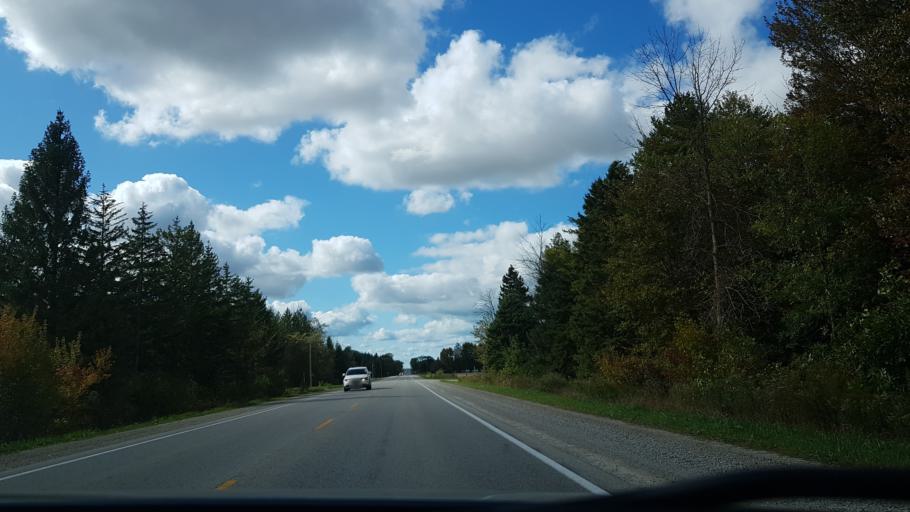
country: CA
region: Ontario
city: South Huron
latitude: 43.3540
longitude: -81.5577
